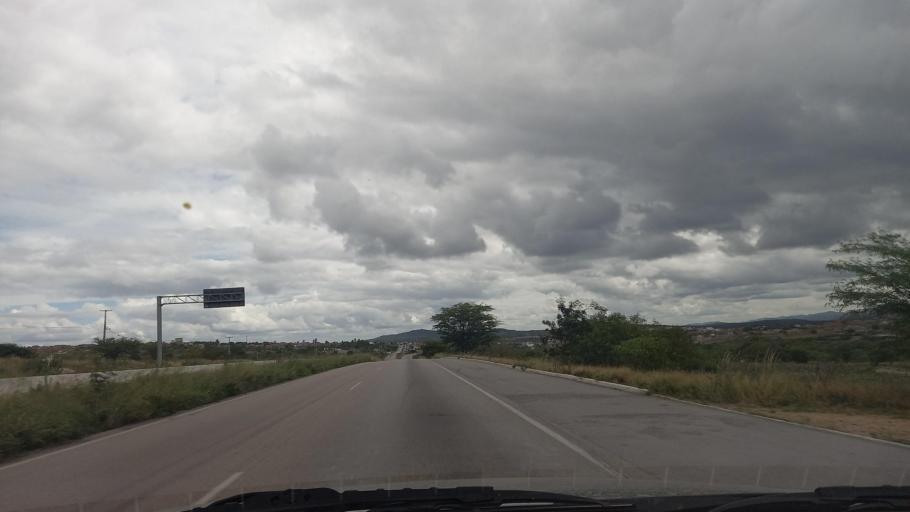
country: BR
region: Pernambuco
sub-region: Caruaru
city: Caruaru
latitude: -8.3259
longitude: -36.1141
